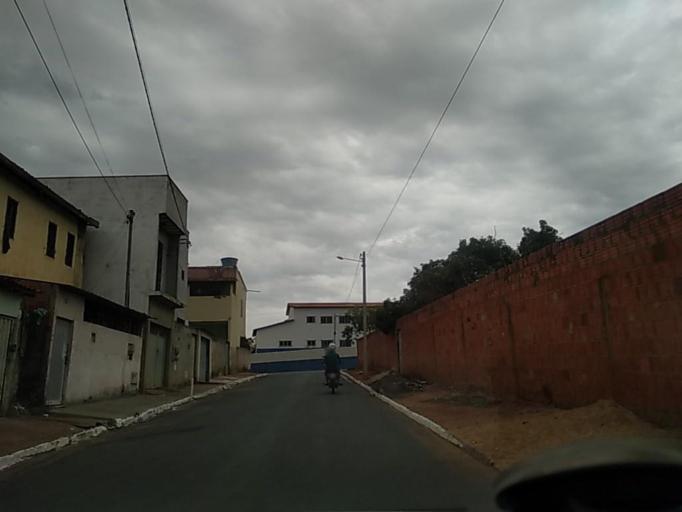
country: BR
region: Bahia
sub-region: Caetite
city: Caetite
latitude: -14.0548
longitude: -42.4826
